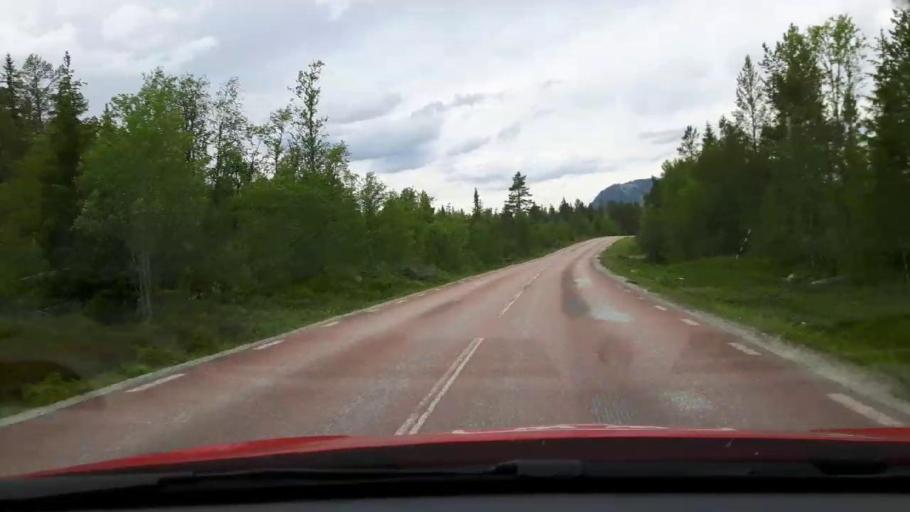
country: NO
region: Hedmark
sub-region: Engerdal
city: Engerdal
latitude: 62.5083
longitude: 12.6115
